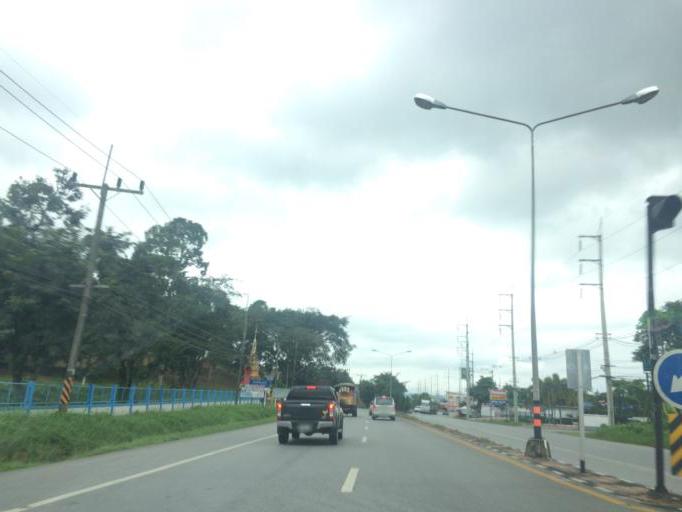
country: TH
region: Chiang Rai
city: Mae Chan
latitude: 20.1288
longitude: 99.8654
